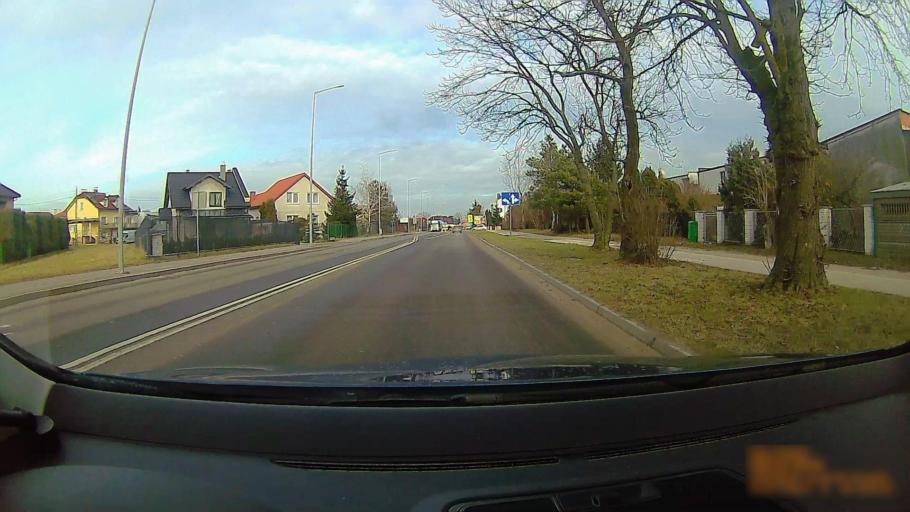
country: PL
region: Greater Poland Voivodeship
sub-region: Konin
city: Konin
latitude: 52.1991
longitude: 18.2422
